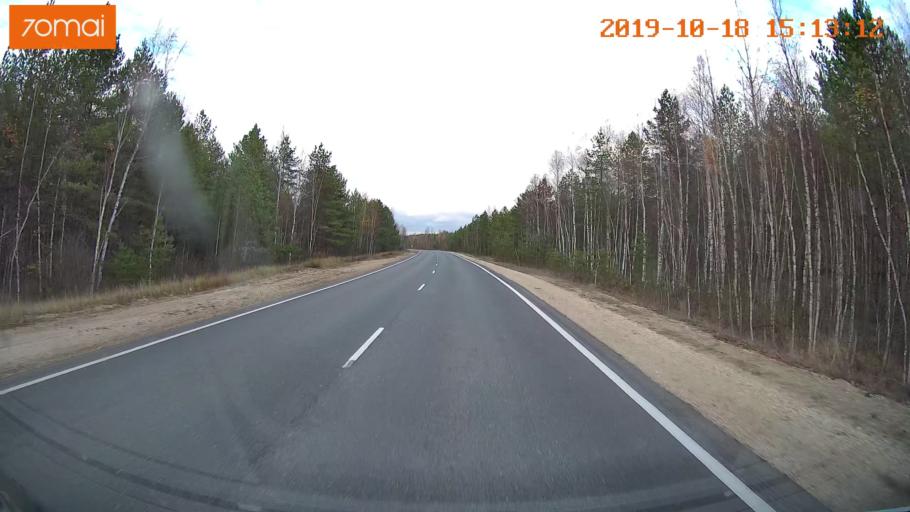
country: RU
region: Vladimir
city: Gus'-Khrustal'nyy
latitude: 55.5835
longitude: 40.7137
